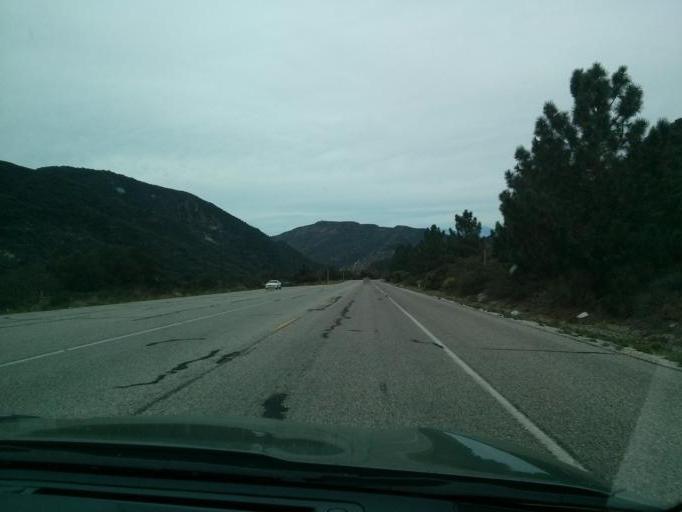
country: US
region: California
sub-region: San Bernardino County
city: Yucaipa
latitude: 34.0991
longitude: -116.9829
